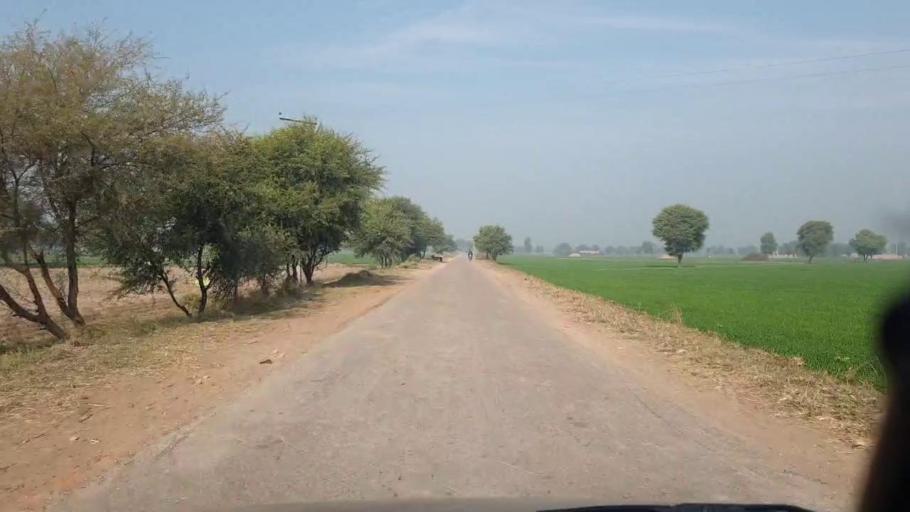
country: PK
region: Sindh
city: Shahdadpur
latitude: 26.0027
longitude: 68.5544
